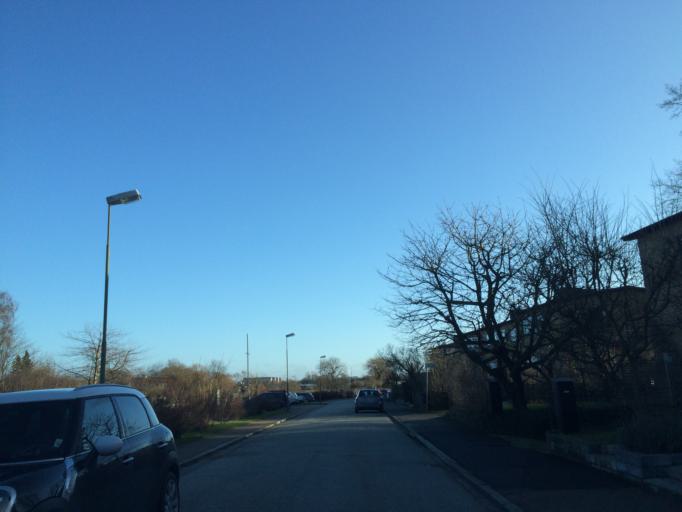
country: SE
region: Skane
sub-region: Malmo
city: Bunkeflostrand
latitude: 55.5760
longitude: 12.9472
